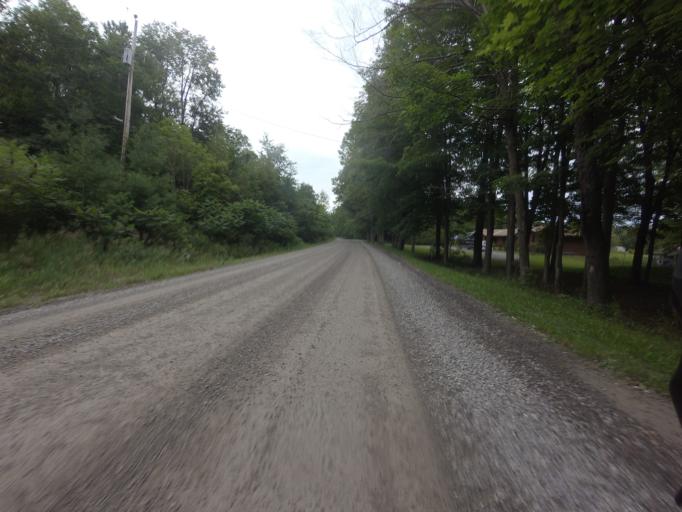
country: CA
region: Ontario
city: Carleton Place
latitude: 45.1533
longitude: -76.2466
